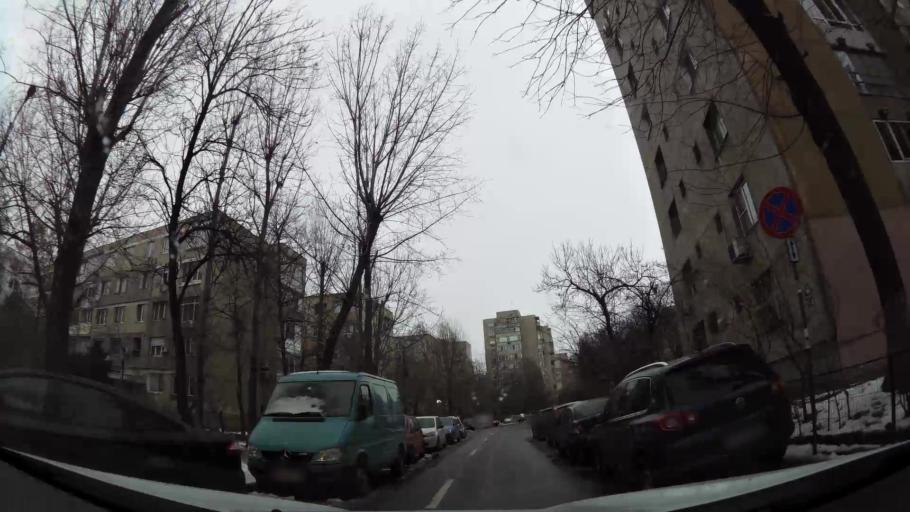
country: RO
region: Ilfov
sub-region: Comuna Chiajna
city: Rosu
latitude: 44.4185
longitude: 26.0217
